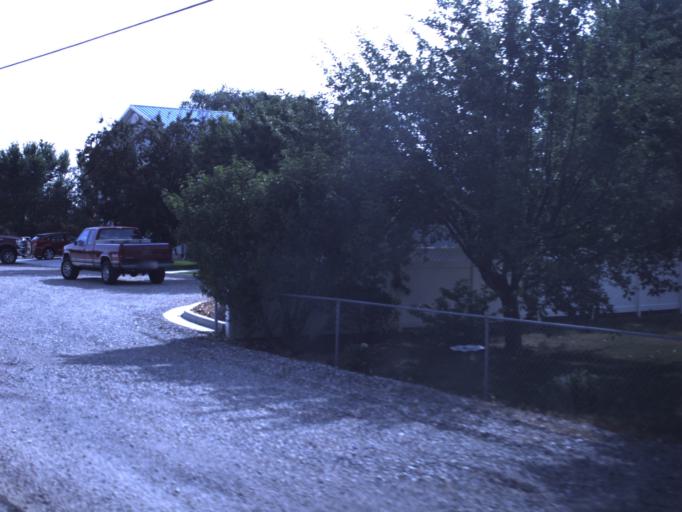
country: US
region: Utah
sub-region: Box Elder County
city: Elwood
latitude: 41.6916
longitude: -112.0900
